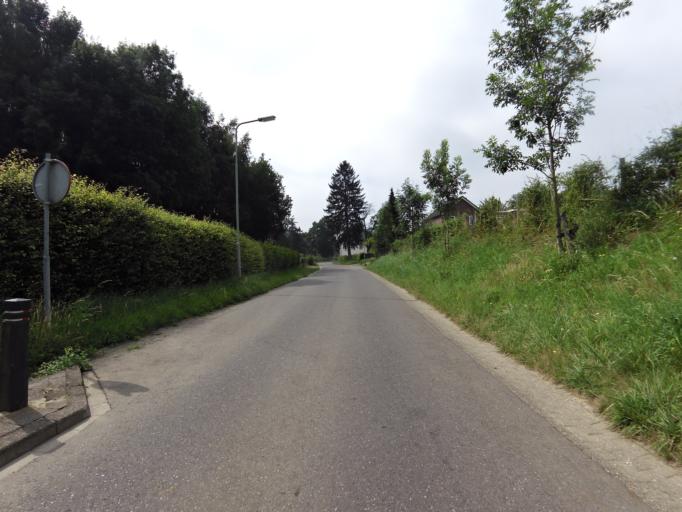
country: NL
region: Limburg
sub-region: Valkenburg aan de Geul
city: Schin op Geul
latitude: 50.8610
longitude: 5.8695
